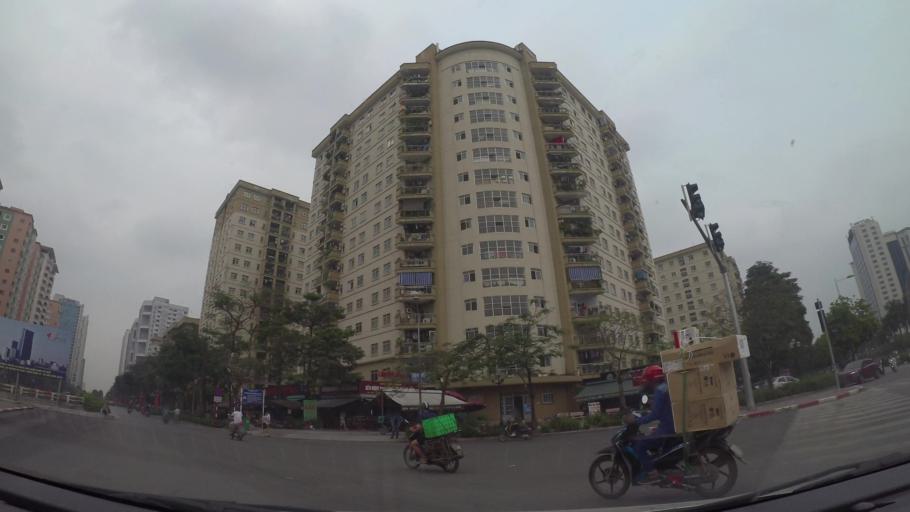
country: VN
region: Ha Noi
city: Cau Dien
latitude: 21.0294
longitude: 105.7642
